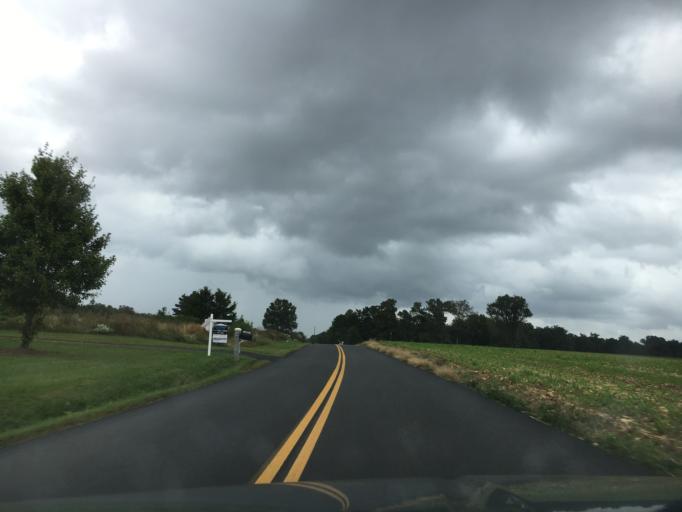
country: US
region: Virginia
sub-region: Amelia County
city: Amelia Court House
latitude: 37.4245
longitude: -77.9584
